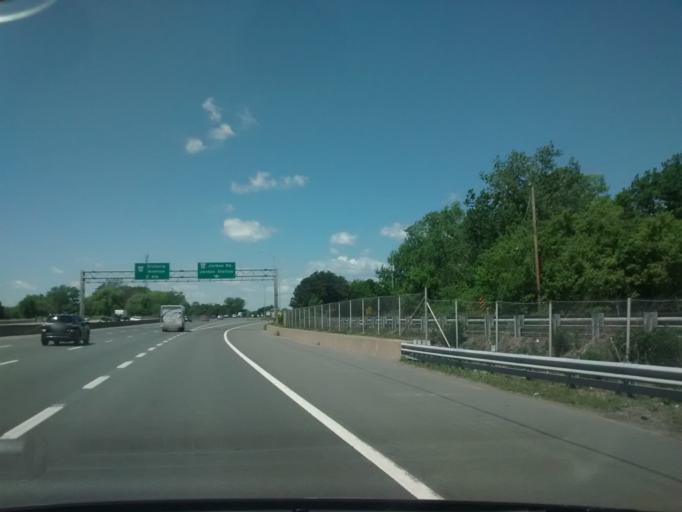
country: CA
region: Ontario
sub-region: Regional Municipality of Niagara
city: St. Catharines
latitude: 43.1794
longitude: -79.3549
